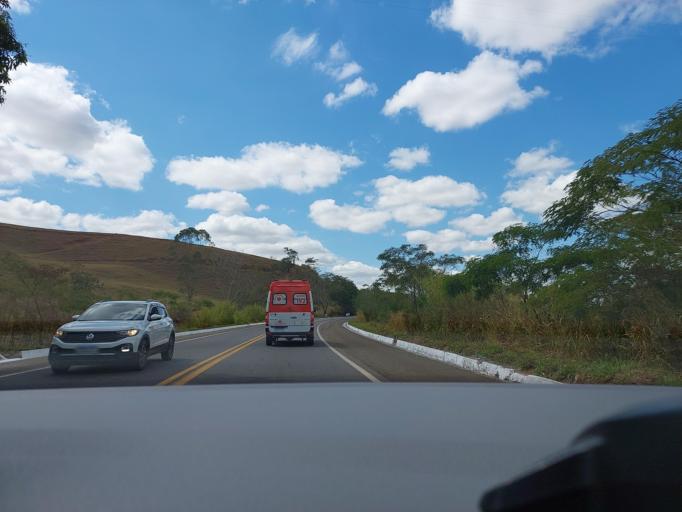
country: BR
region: Minas Gerais
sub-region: Muriae
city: Muriae
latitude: -21.1377
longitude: -42.3044
